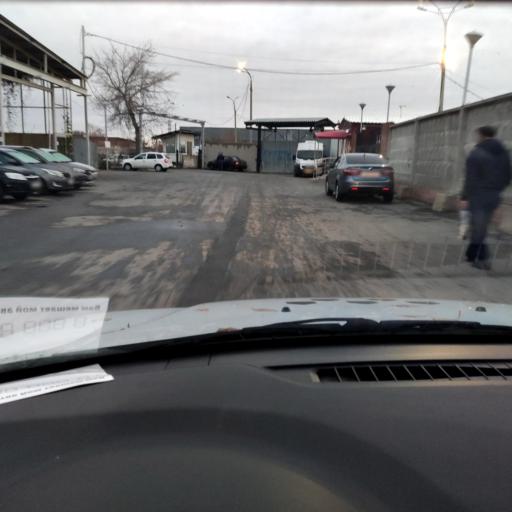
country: RU
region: Samara
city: Tol'yatti
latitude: 53.5478
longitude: 49.4370
